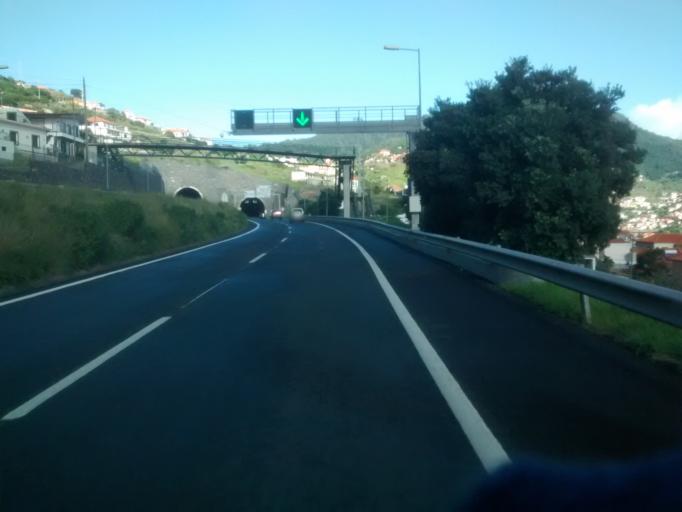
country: PT
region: Madeira
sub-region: Machico
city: Machico
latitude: 32.7210
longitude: -16.7747
